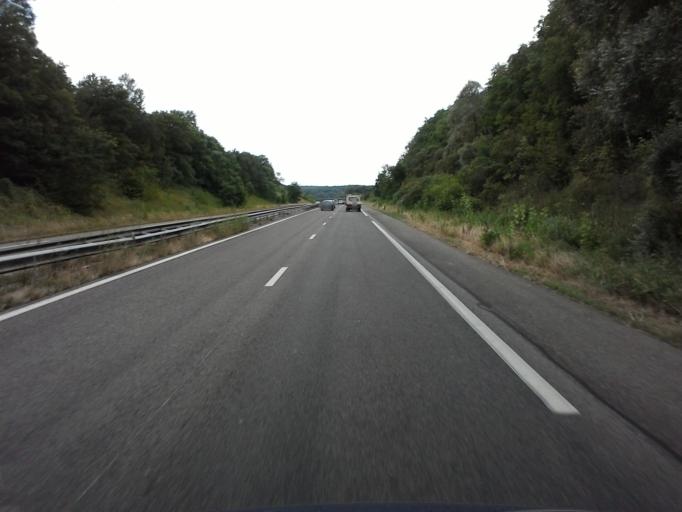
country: FR
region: Lorraine
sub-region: Departement de Meurthe-et-Moselle
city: Bayon
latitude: 48.4487
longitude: 6.2332
